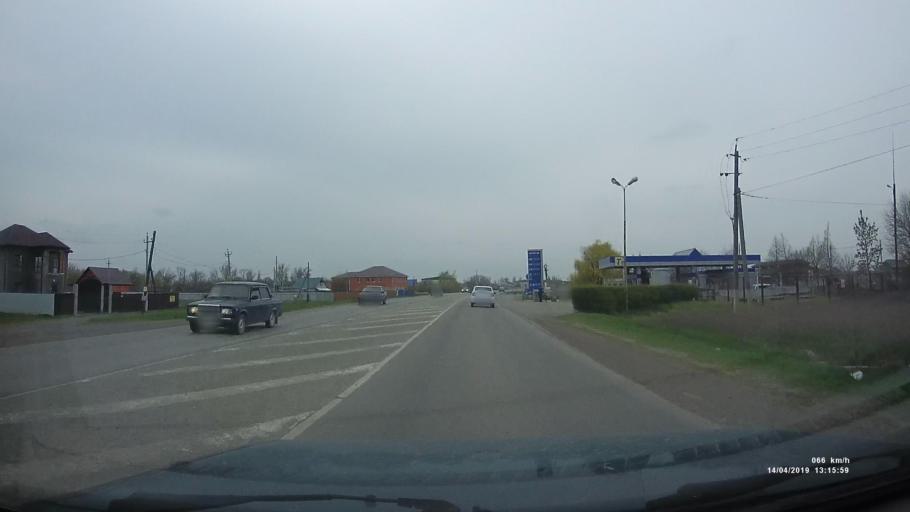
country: RU
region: Rostov
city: Kuleshovka
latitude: 47.0812
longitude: 39.5874
